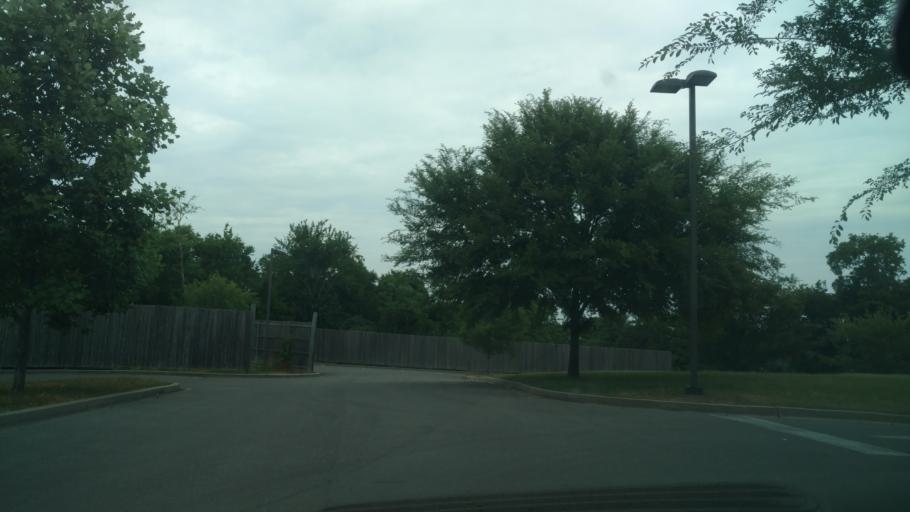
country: US
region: Tennessee
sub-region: Davidson County
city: Nashville
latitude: 36.1992
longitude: -86.7266
